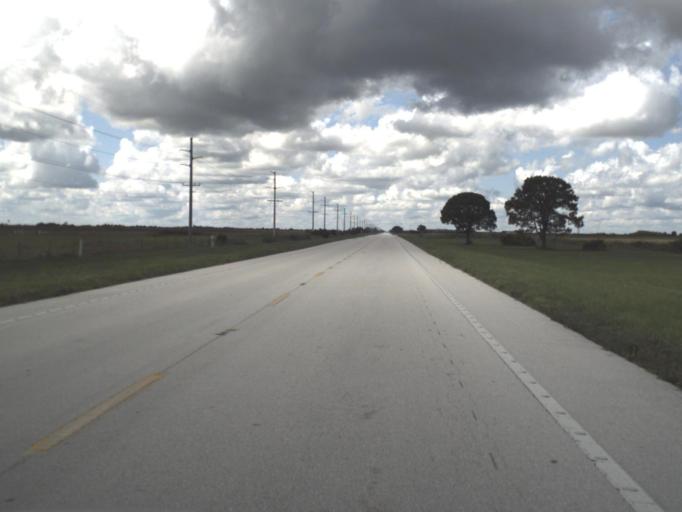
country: US
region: Florida
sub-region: Highlands County
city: Placid Lakes
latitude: 27.2097
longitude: -81.5729
